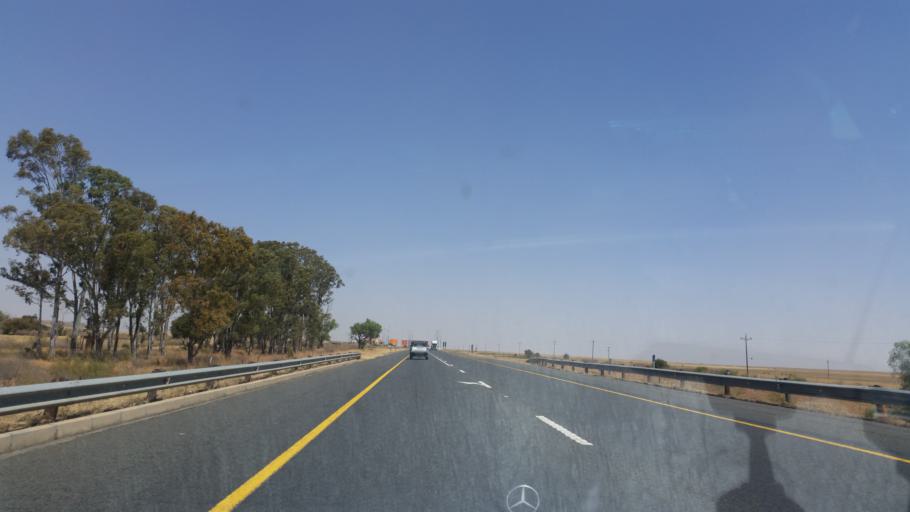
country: ZA
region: Orange Free State
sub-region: Lejweleputswa District Municipality
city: Brandfort
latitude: -28.7922
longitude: 26.6990
